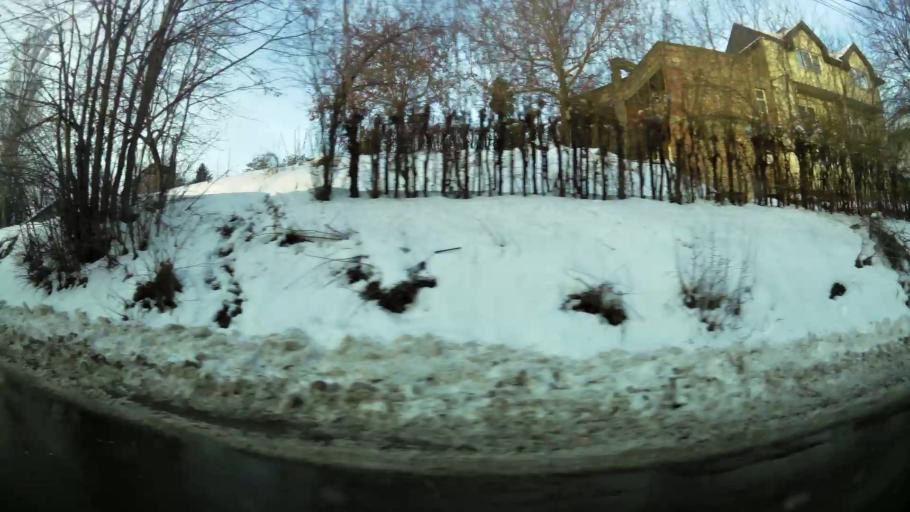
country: RS
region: Central Serbia
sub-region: Belgrade
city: Palilula
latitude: 44.7948
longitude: 20.5116
